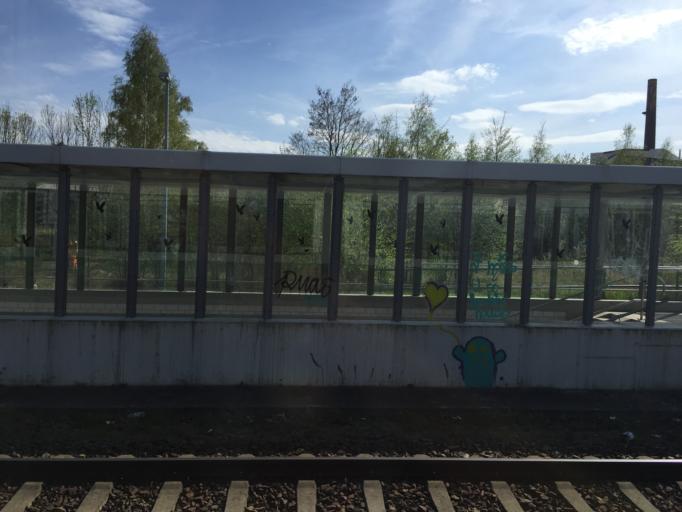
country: DE
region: Saxony
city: Reichenbach
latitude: 51.1355
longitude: 14.7968
